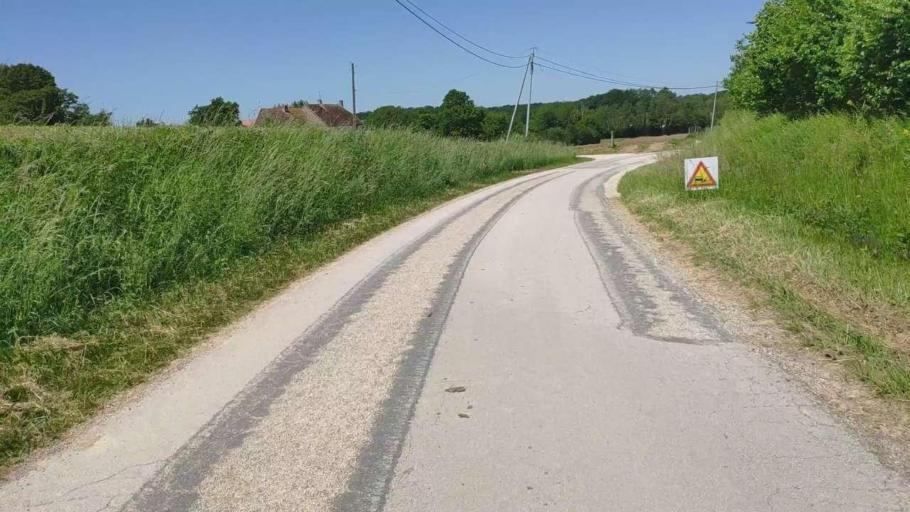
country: FR
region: Franche-Comte
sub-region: Departement du Jura
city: Bletterans
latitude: 46.7568
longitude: 5.4216
